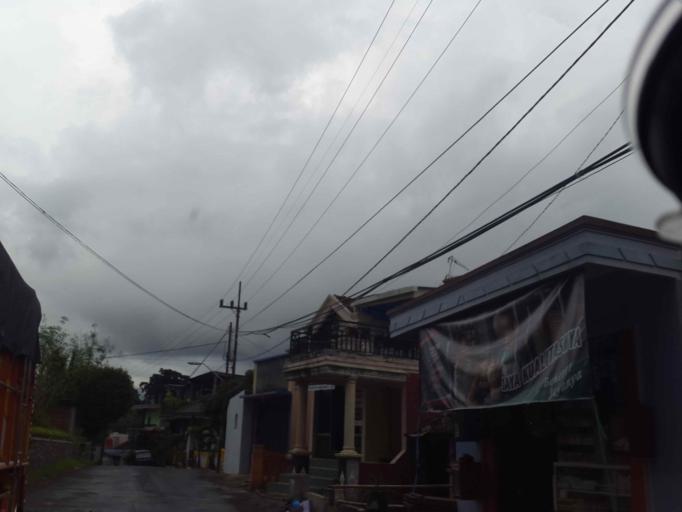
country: ID
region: East Java
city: Batu
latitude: -7.8638
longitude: 112.5363
